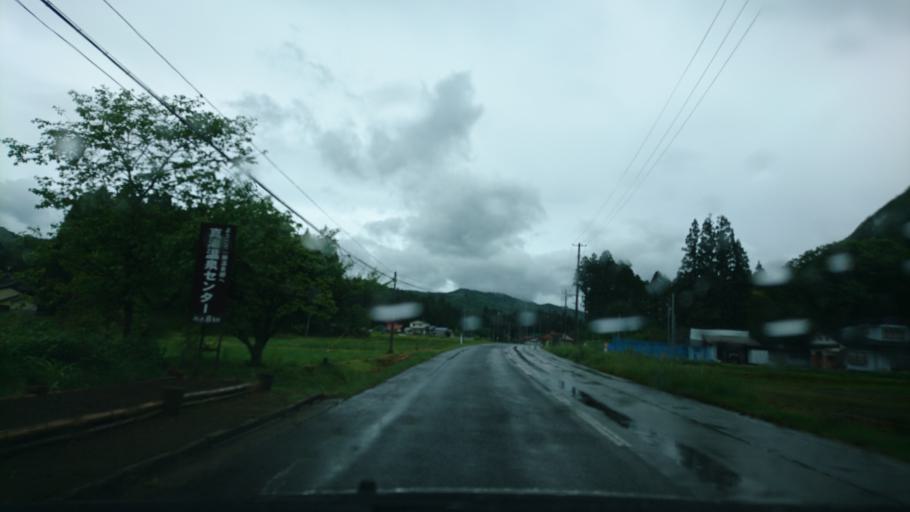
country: JP
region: Iwate
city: Ichinoseki
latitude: 38.9831
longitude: 140.9145
